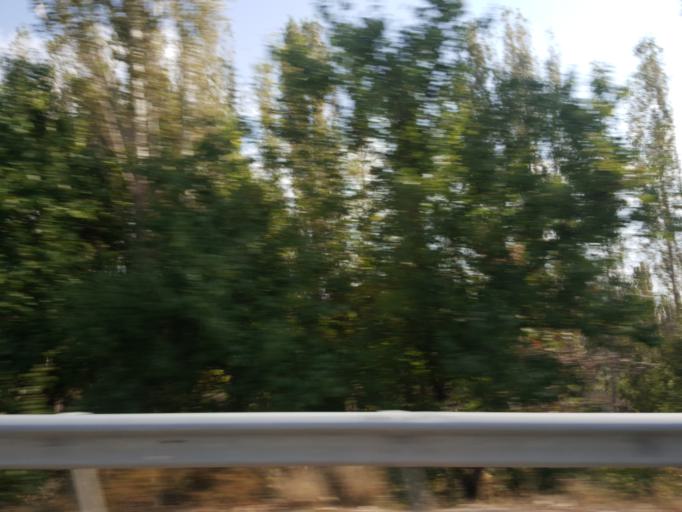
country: TR
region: Corum
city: Sungurlu
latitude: 40.1845
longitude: 34.4924
